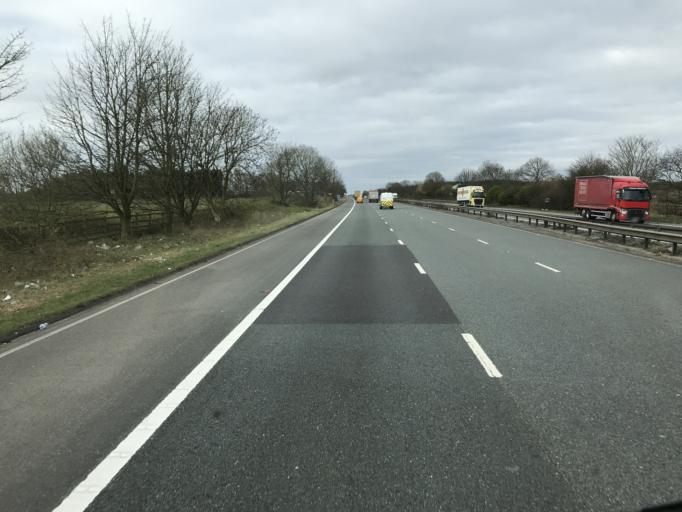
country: GB
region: England
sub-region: Warrington
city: Burtonwood
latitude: 53.4107
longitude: -2.7008
